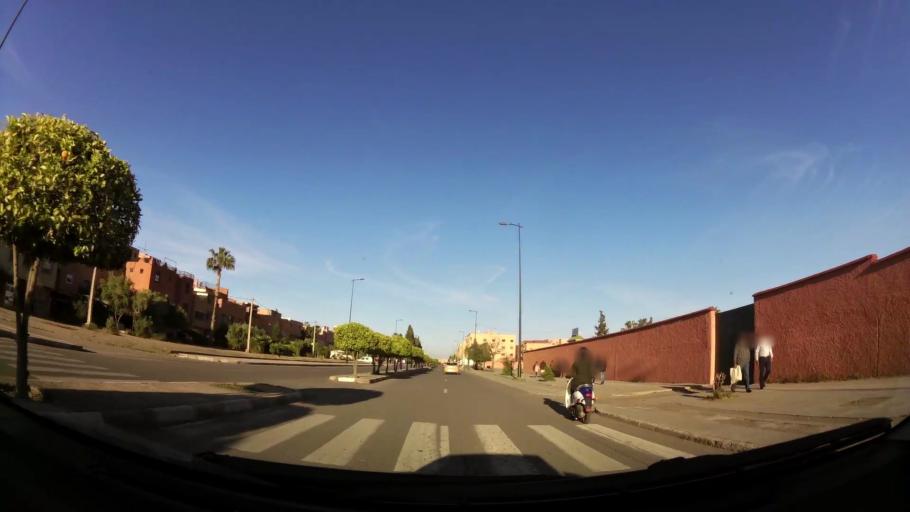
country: MA
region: Marrakech-Tensift-Al Haouz
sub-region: Marrakech
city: Marrakesh
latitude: 31.6220
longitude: -8.0541
